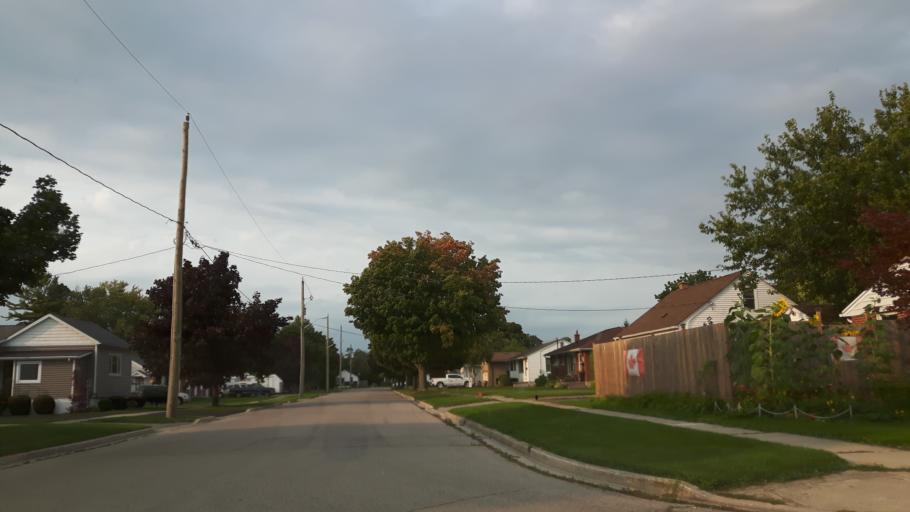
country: CA
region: Ontario
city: Goderich
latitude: 43.7373
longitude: -81.7203
